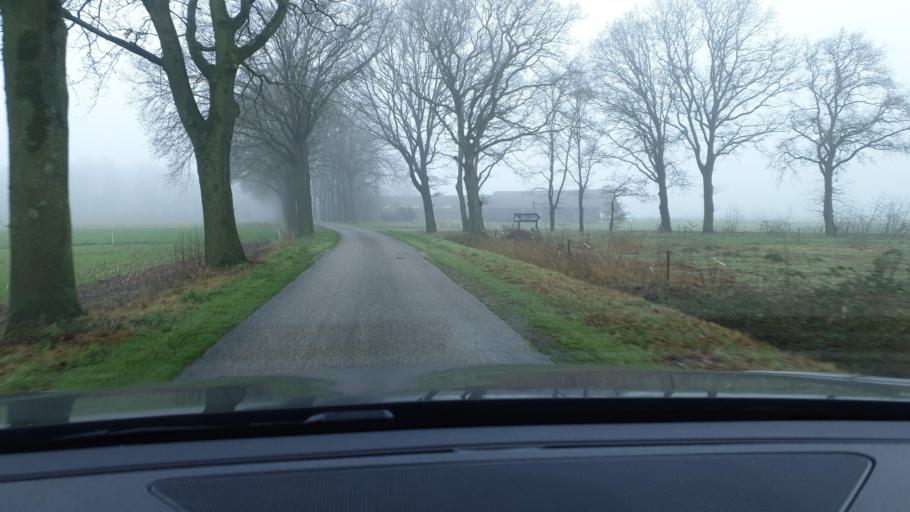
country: NL
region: North Brabant
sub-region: Gemeente Asten
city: Asten
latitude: 51.3661
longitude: 5.8444
